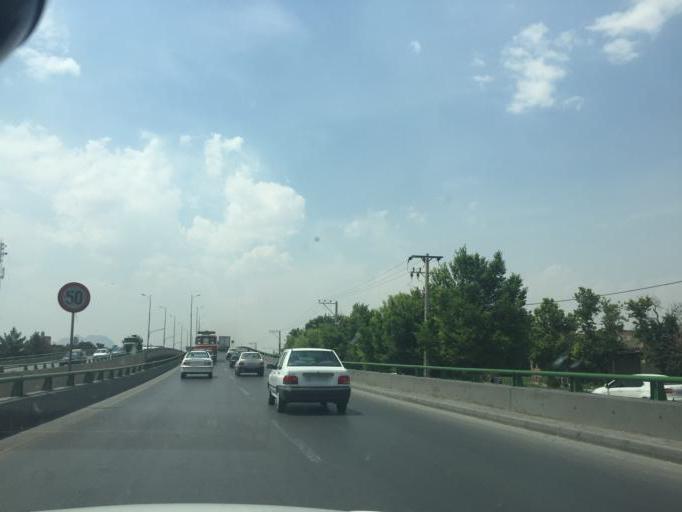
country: IR
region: Isfahan
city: Rehnan
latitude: 32.6829
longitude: 51.6400
